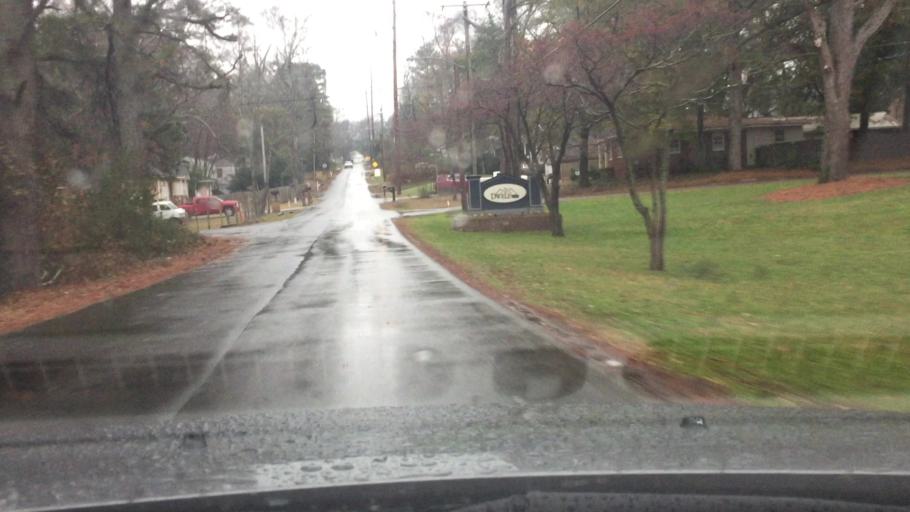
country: US
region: Georgia
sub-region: Cobb County
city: Fair Oaks
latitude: 33.9110
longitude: -84.5435
